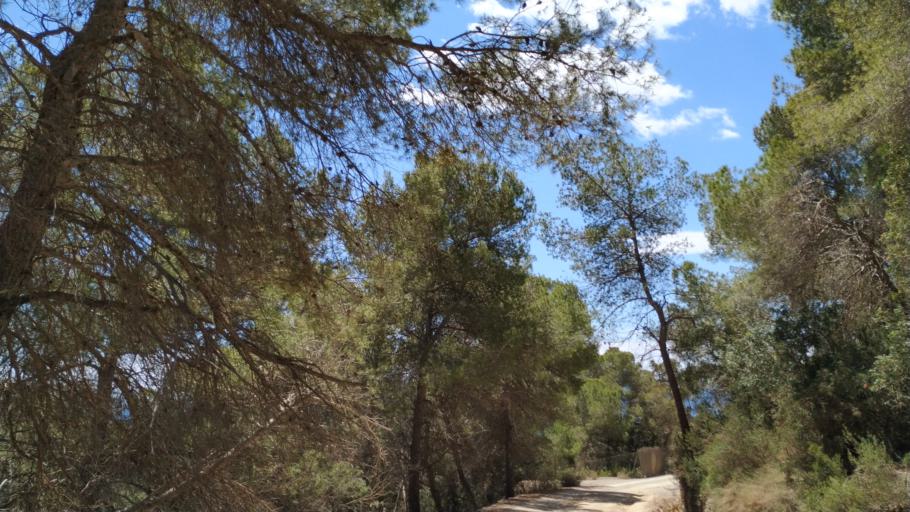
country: ES
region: Balearic Islands
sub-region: Illes Balears
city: Ibiza
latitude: 38.9224
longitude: 1.4748
